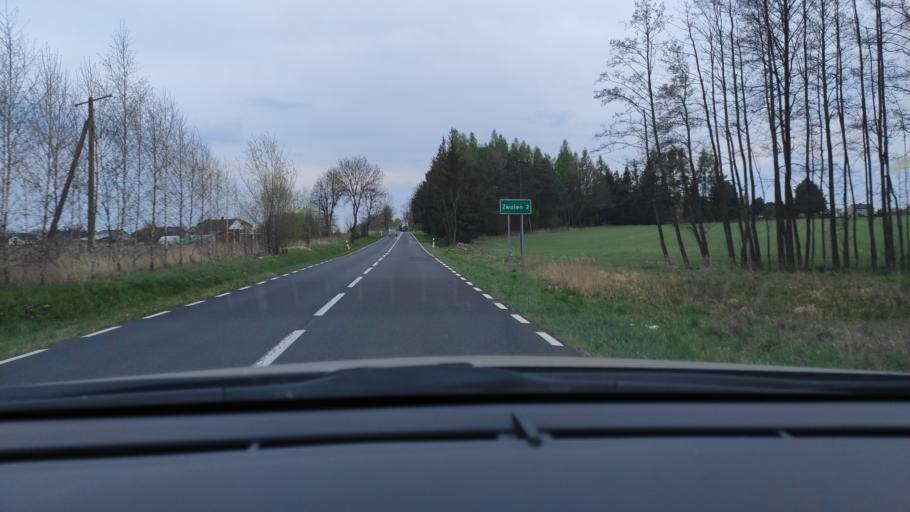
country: PL
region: Masovian Voivodeship
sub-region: Powiat zwolenski
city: Zwolen
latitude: 51.3862
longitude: 21.5541
